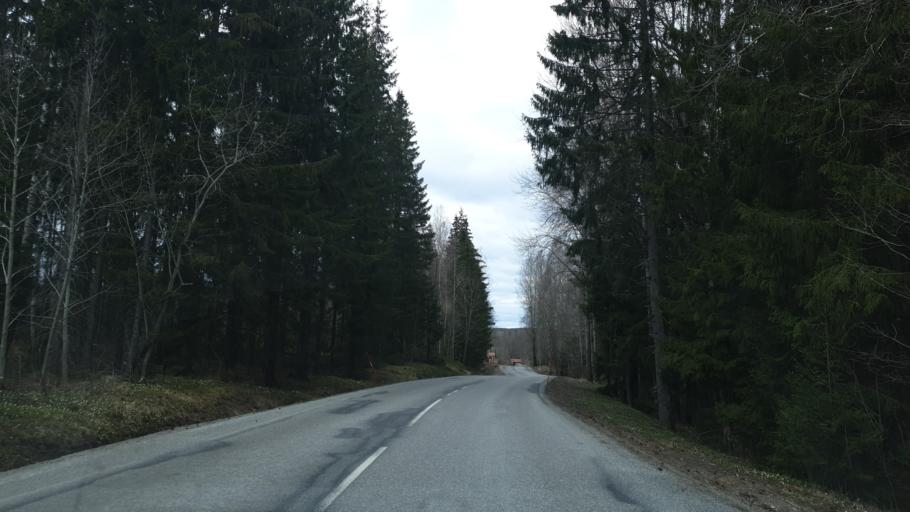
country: SE
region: OErebro
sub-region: Nora Kommun
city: Nora
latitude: 59.5470
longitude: 15.0294
